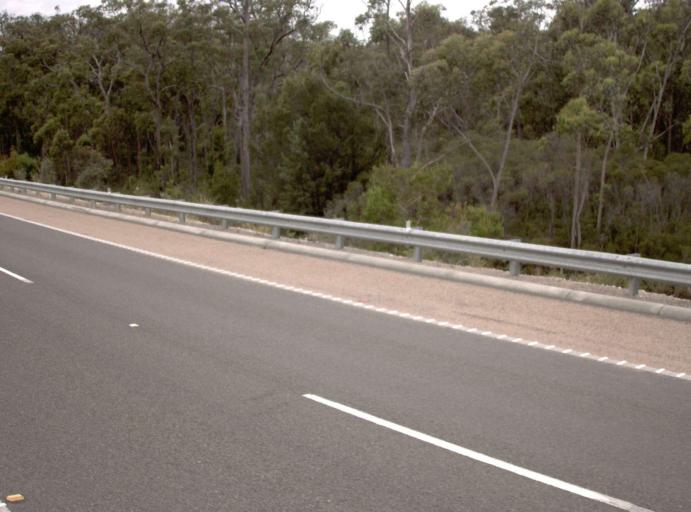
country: AU
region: Victoria
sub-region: East Gippsland
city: Lakes Entrance
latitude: -37.6940
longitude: 147.9979
